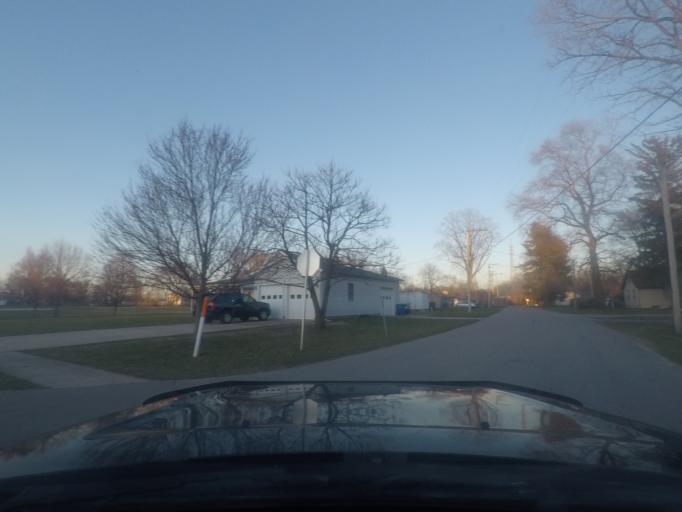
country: US
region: Indiana
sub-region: LaPorte County
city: Kingsford Heights
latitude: 41.5243
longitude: -86.7011
